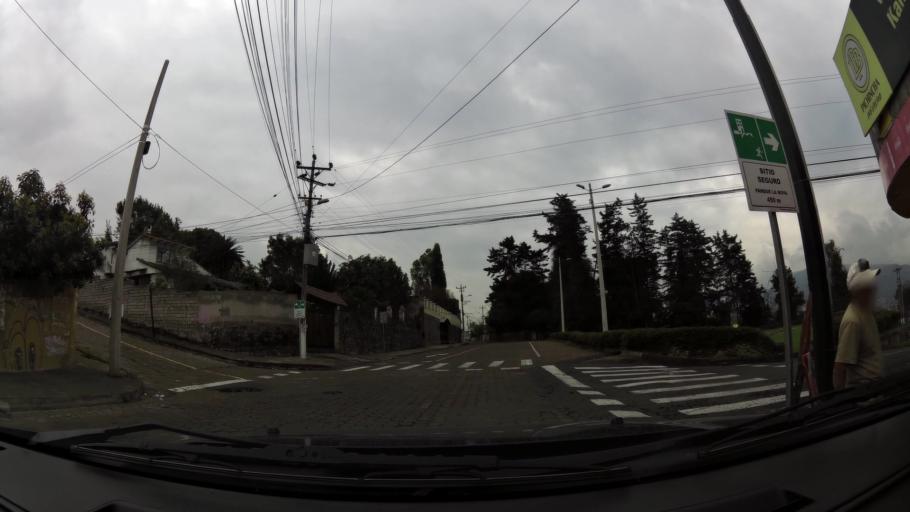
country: EC
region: Pichincha
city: Sangolqui
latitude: -0.3002
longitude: -78.4745
